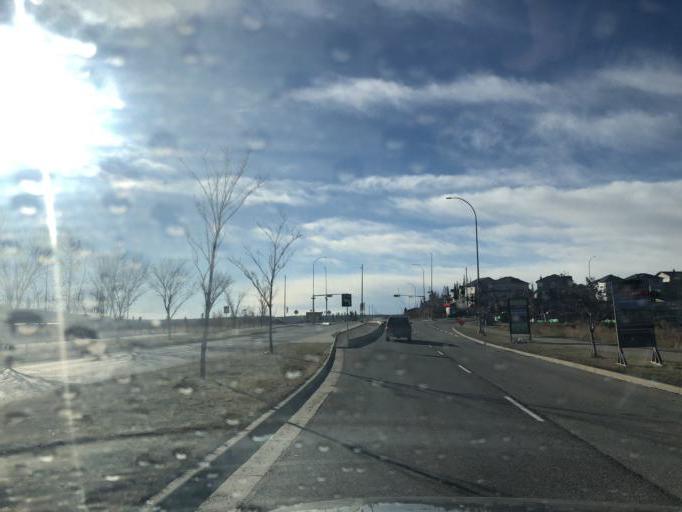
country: CA
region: Alberta
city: Calgary
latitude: 51.0394
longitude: -114.2111
